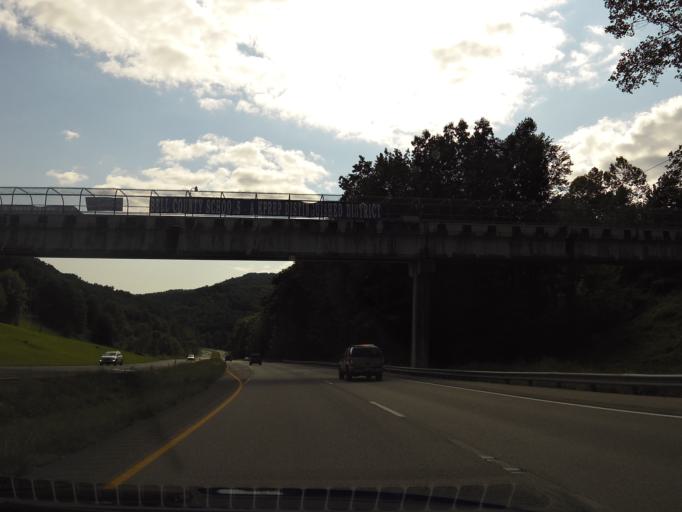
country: US
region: Kentucky
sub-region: Bell County
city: Pineville
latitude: 36.7131
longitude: -83.6928
